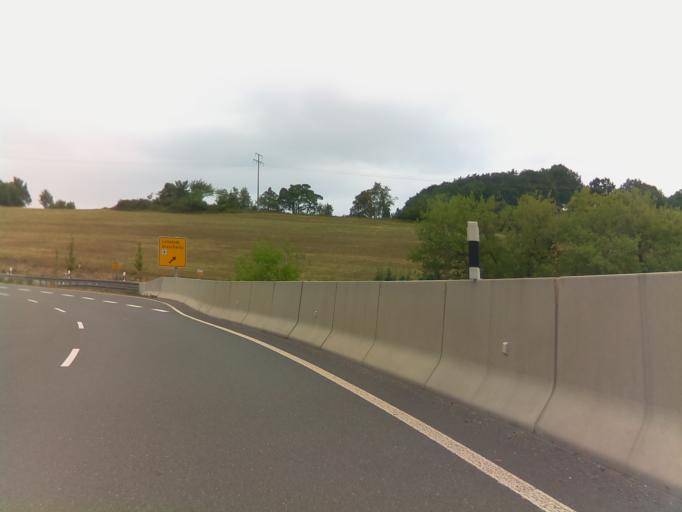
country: DE
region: Thuringia
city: Bad Blankenburg
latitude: 50.7304
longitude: 11.2548
